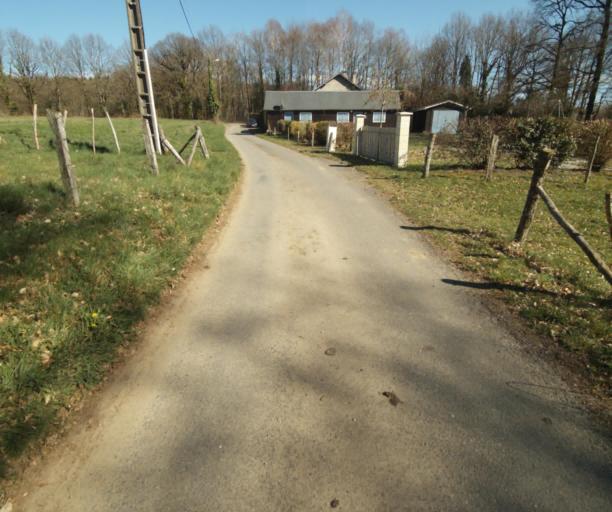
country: FR
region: Limousin
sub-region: Departement de la Correze
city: Chamboulive
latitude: 45.4712
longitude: 1.7387
